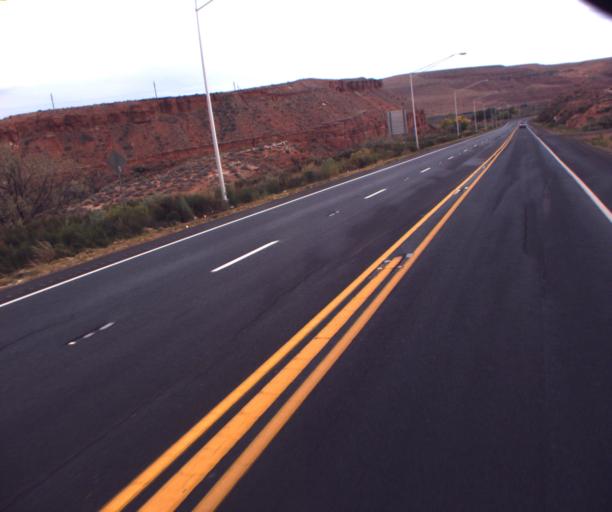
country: US
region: Arizona
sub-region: Coconino County
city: Tuba City
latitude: 36.1157
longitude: -111.2322
